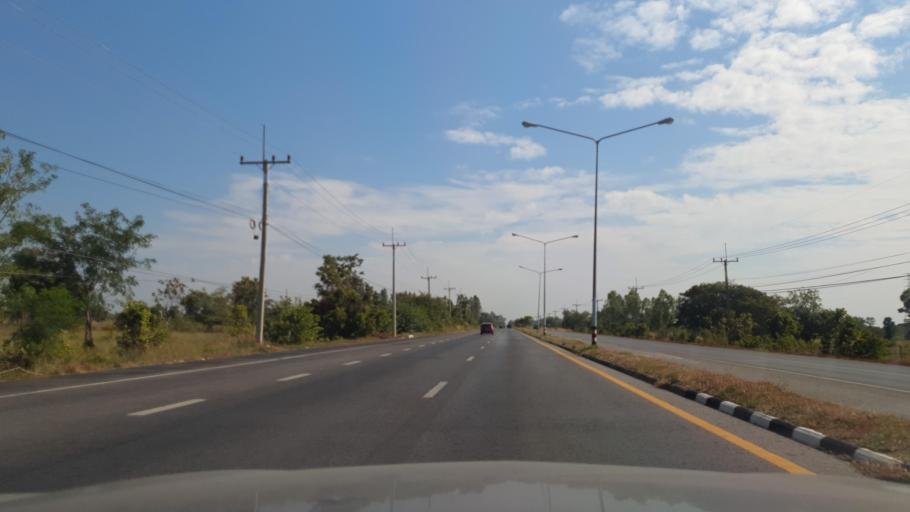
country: TH
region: Maha Sarakham
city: Kantharawichai
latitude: 16.3843
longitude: 103.2280
